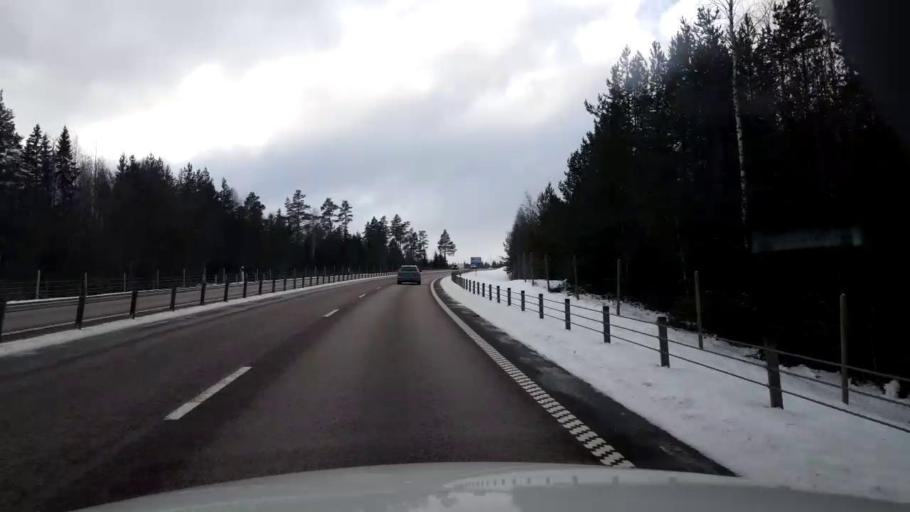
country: SE
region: Gaevleborg
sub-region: Hudiksvalls Kommun
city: Hudiksvall
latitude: 61.7956
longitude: 17.1671
